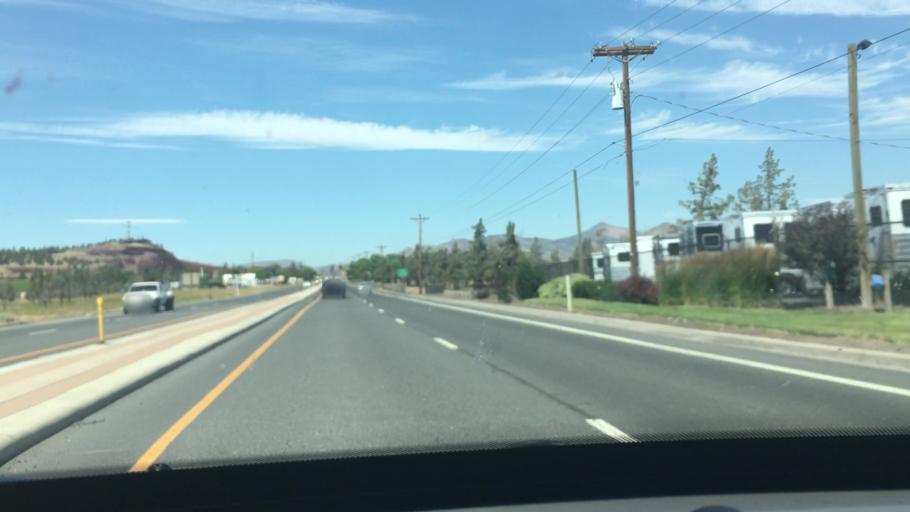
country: US
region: Oregon
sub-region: Deschutes County
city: Redmond
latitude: 44.3051
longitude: -121.1730
